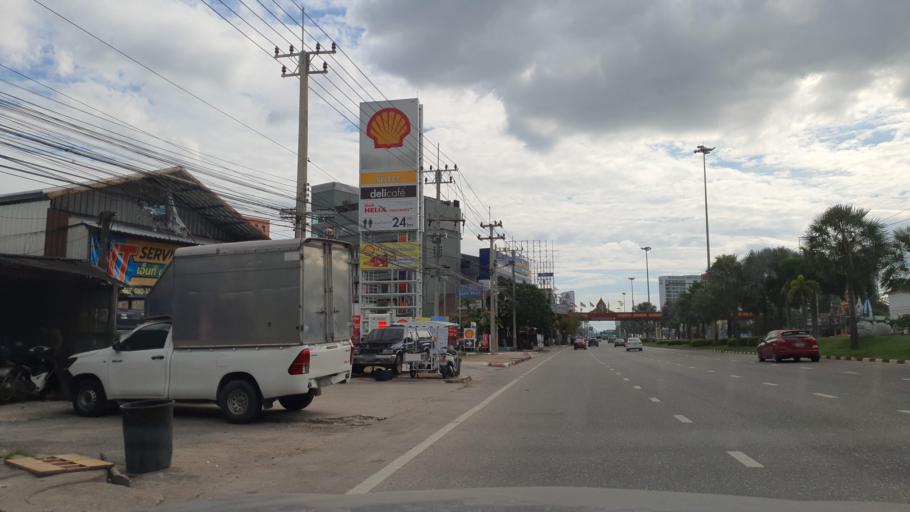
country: TH
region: Chon Buri
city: Phatthaya
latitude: 12.9611
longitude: 100.9091
